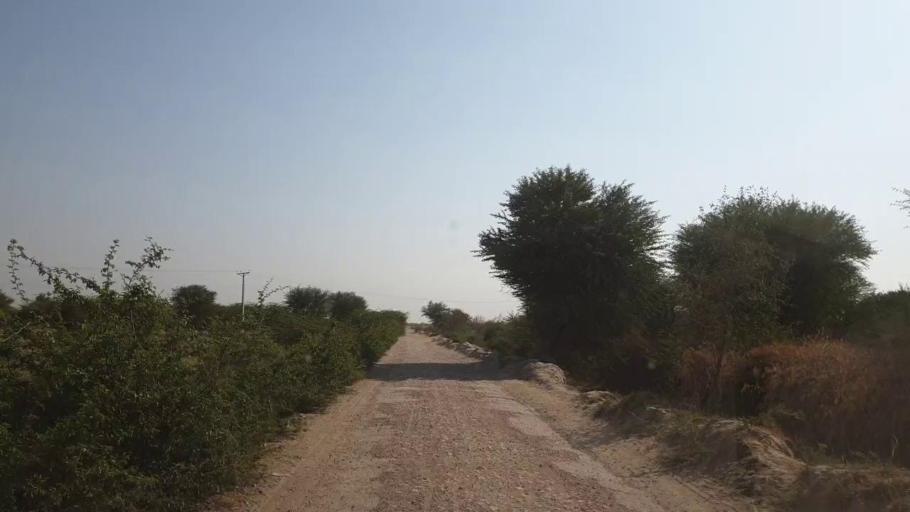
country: PK
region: Sindh
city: Nabisar
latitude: 25.0260
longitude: 69.4946
